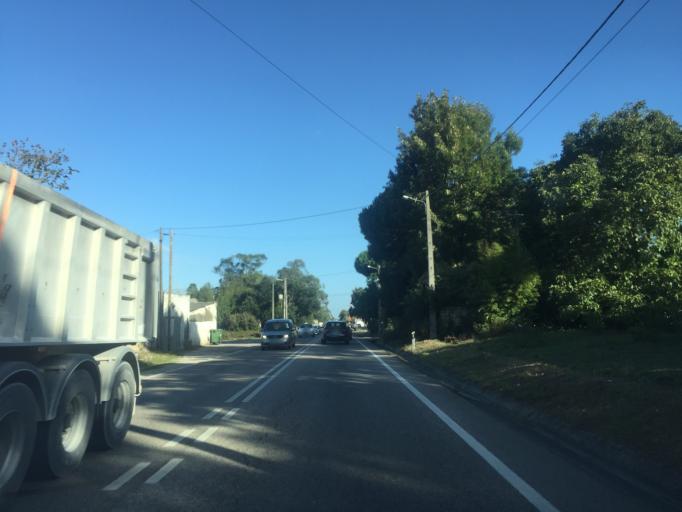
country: PT
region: Leiria
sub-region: Alcobaca
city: Benedita
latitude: 39.3967
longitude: -8.9601
